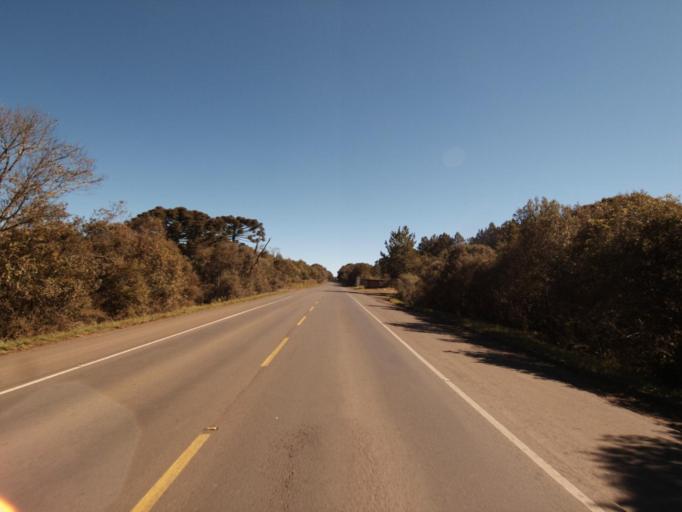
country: BR
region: Santa Catarina
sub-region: Concordia
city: Concordia
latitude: -26.9163
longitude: -51.8981
